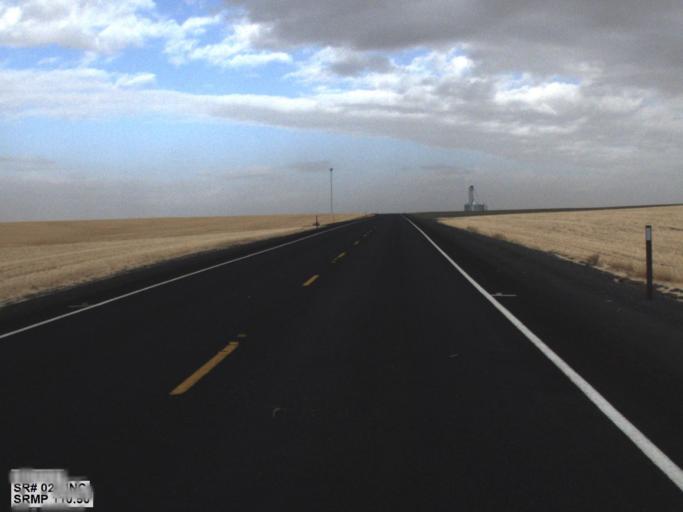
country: US
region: Washington
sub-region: Adams County
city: Ritzville
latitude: 47.4129
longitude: -118.3721
